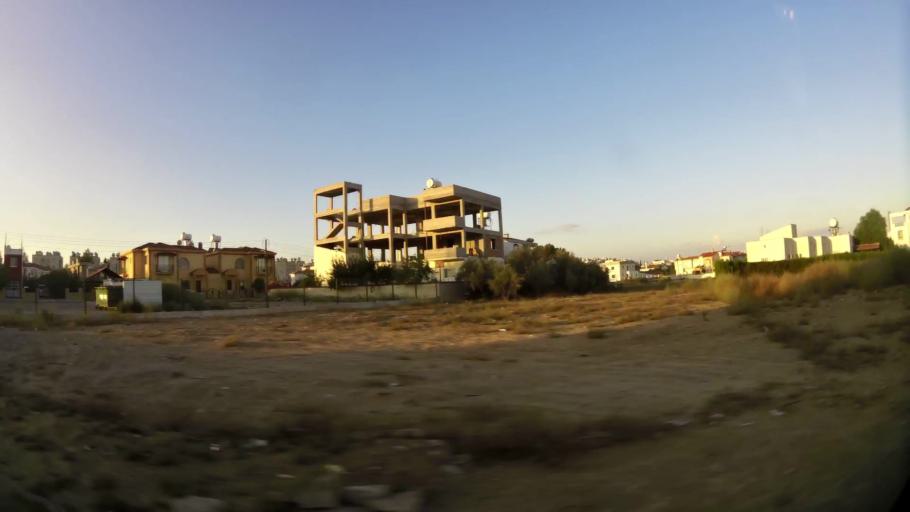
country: CY
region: Lefkosia
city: Nicosia
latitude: 35.1912
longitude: 33.3249
